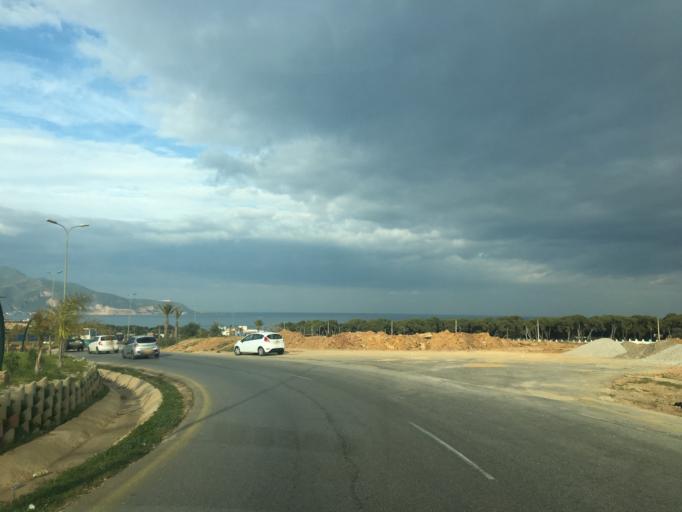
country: DZ
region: Tipaza
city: Tipasa
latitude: 36.5898
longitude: 2.4689
